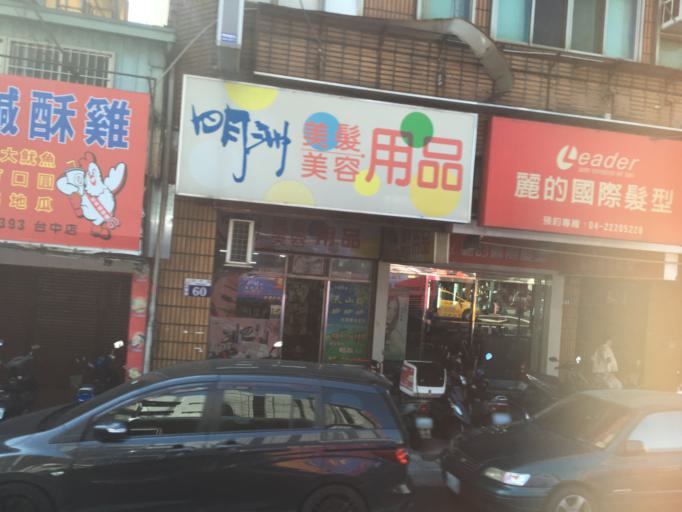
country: TW
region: Taiwan
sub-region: Taichung City
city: Taichung
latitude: 24.1344
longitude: 120.6829
